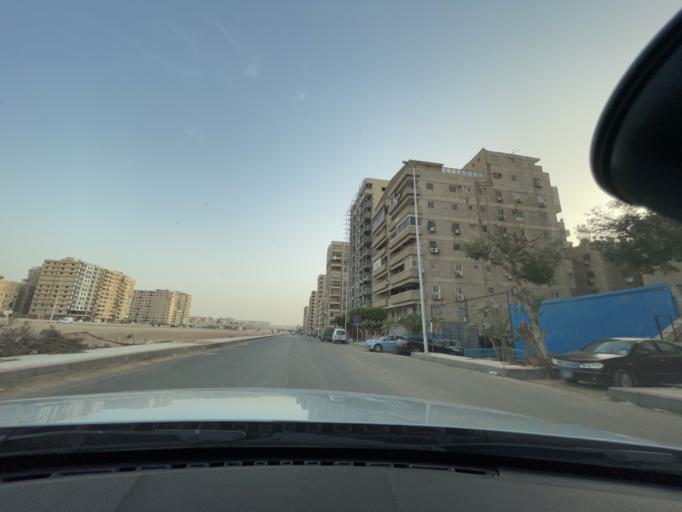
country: EG
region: Muhafazat al Qahirah
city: Cairo
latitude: 30.0518
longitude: 31.3690
